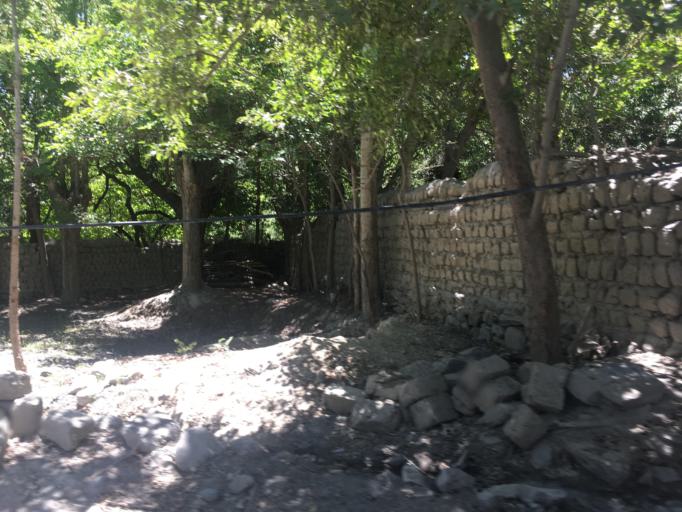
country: PK
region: Gilgit-Baltistan
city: Skardu
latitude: 35.3000
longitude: 75.5495
